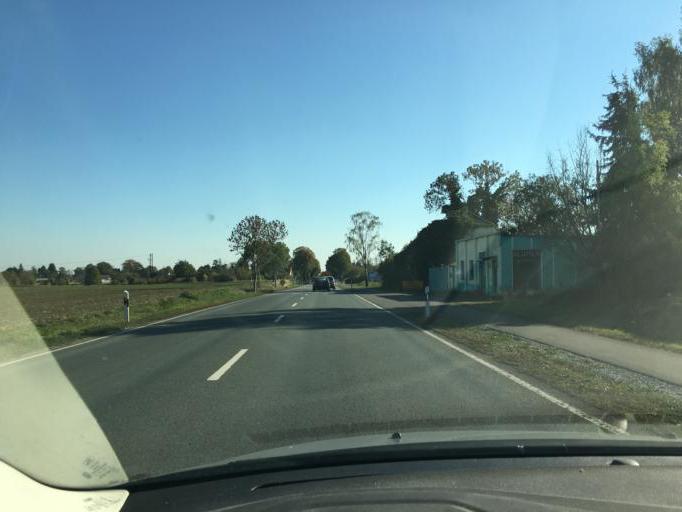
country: DE
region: Saxony-Anhalt
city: Forderstedt
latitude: 51.9055
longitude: 11.6252
